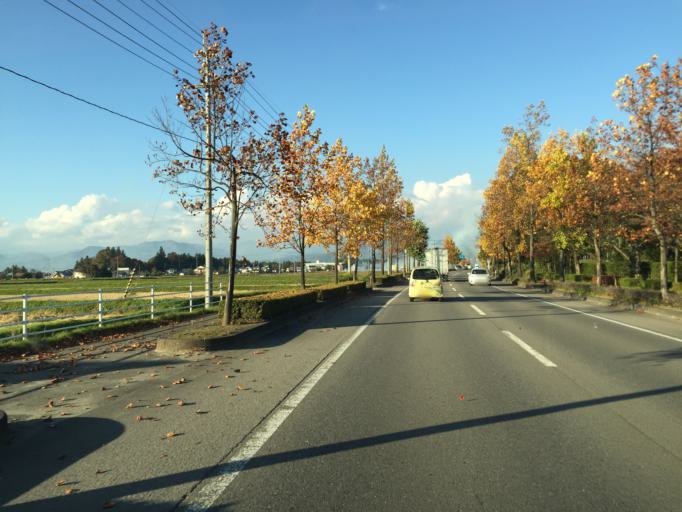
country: JP
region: Fukushima
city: Kitakata
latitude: 37.6598
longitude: 139.8865
